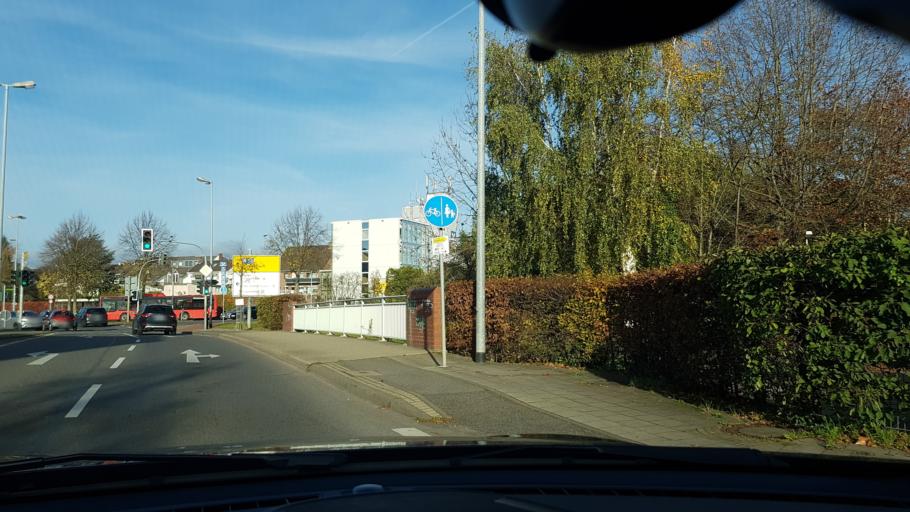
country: DE
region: North Rhine-Westphalia
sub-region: Regierungsbezirk Dusseldorf
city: Grevenbroich
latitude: 51.0899
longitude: 6.5836
